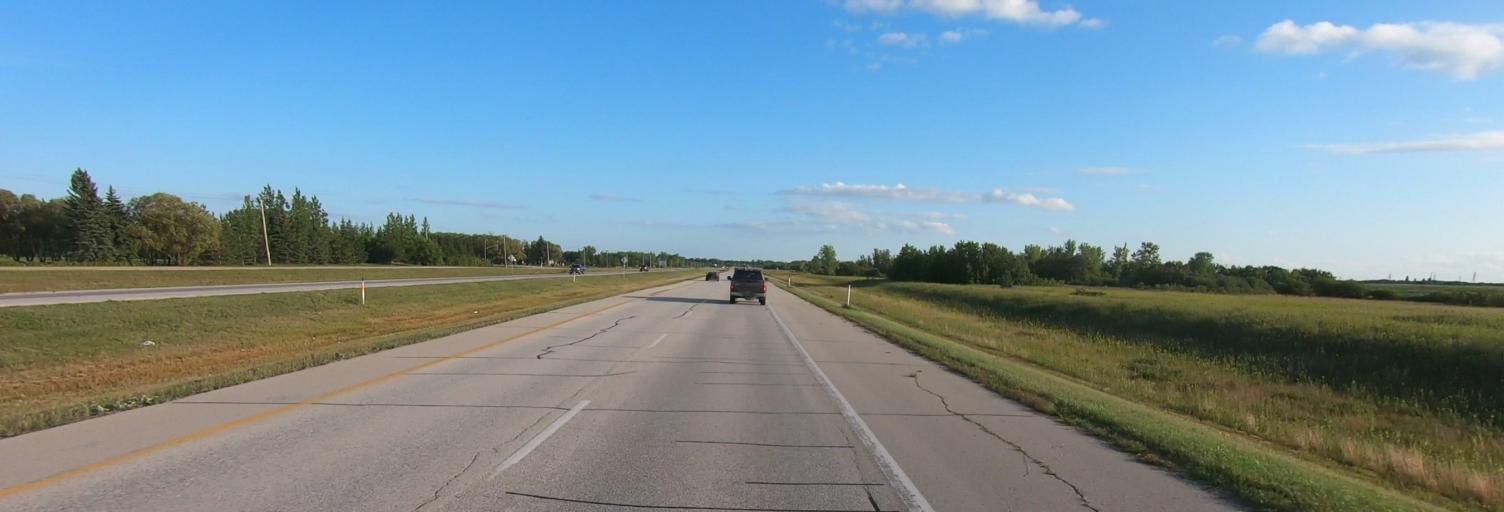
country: CA
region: Manitoba
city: Selkirk
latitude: 49.9883
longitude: -96.9769
